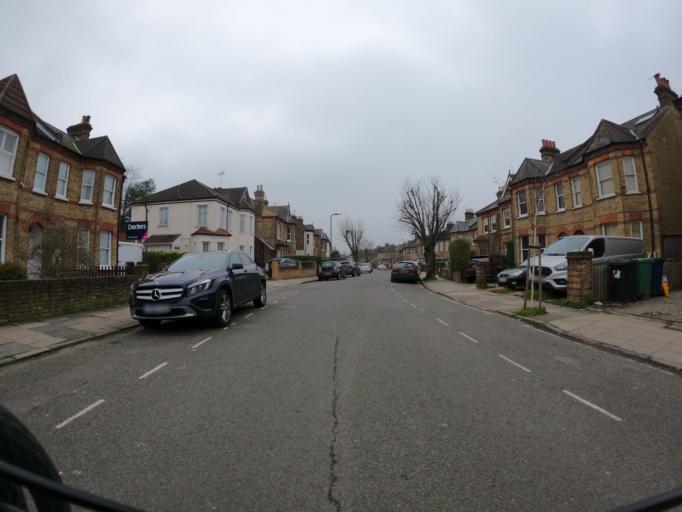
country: GB
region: England
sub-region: Greater London
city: Ealing
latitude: 51.5078
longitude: -0.3267
